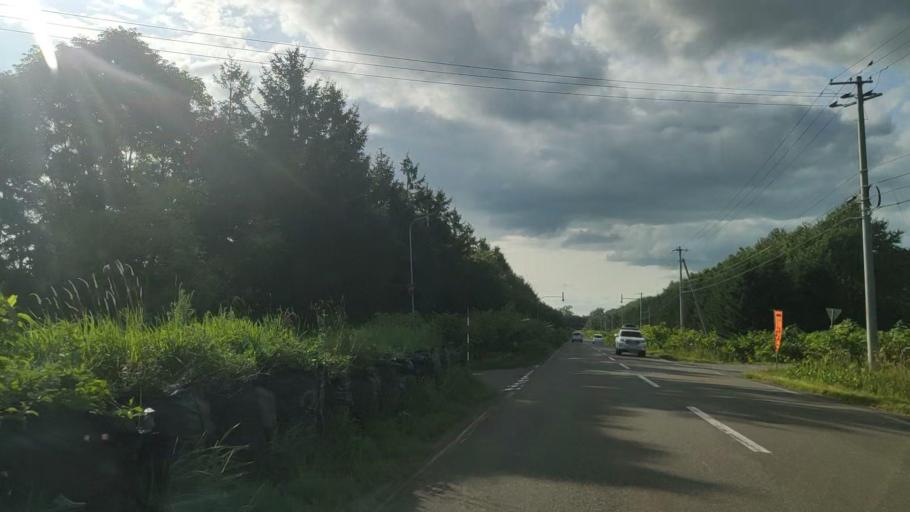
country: JP
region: Hokkaido
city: Makubetsu
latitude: 44.9015
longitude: 141.9101
